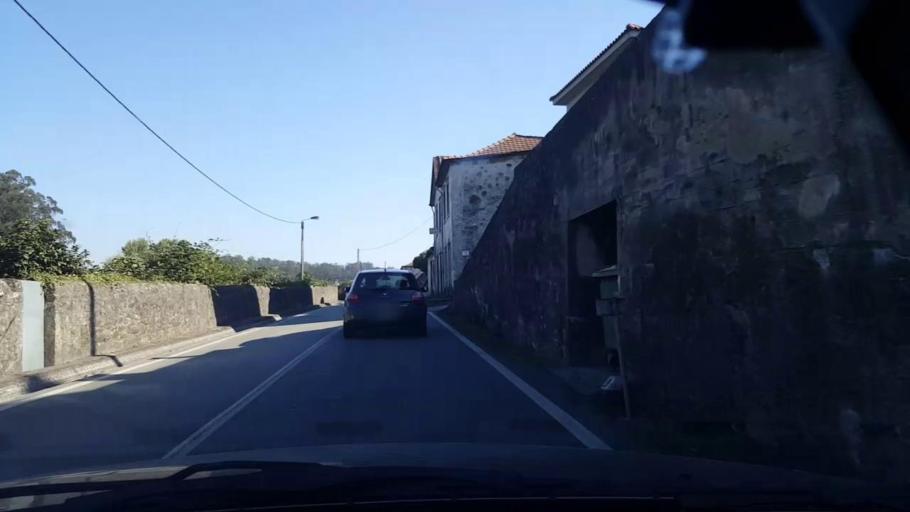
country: PT
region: Porto
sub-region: Vila do Conde
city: Arvore
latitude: 41.3314
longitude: -8.6629
